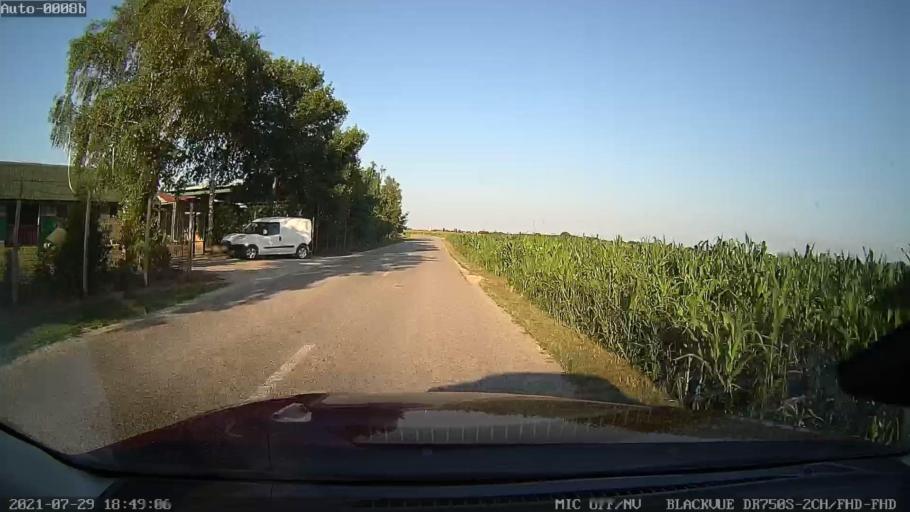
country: HR
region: Varazdinska
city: Nedeljanec
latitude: 46.3106
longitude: 16.3001
